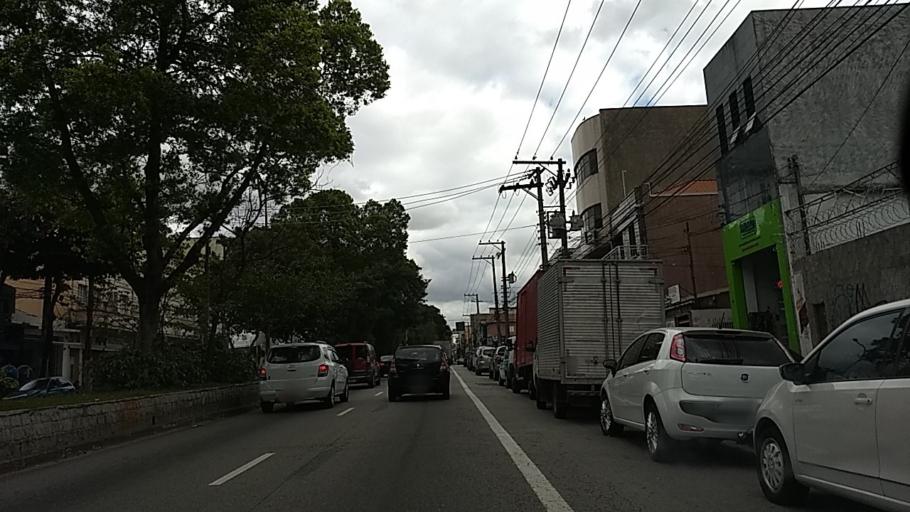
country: BR
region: Sao Paulo
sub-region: Sao Paulo
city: Sao Paulo
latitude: -23.5282
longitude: -46.6132
